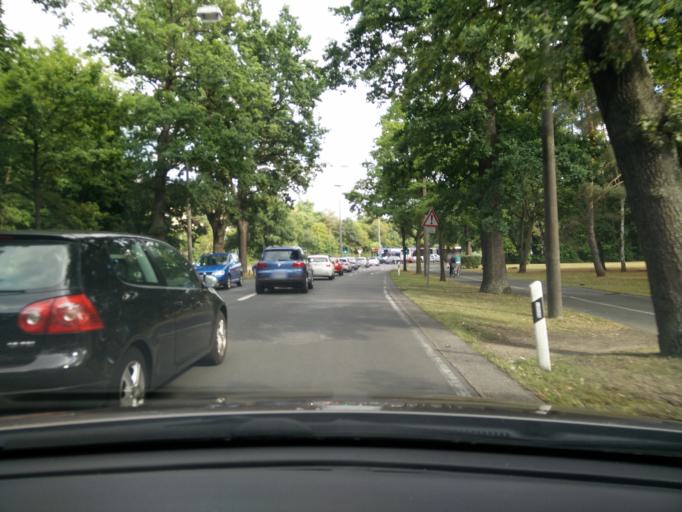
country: DE
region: Bavaria
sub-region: Regierungsbezirk Mittelfranken
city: Erlangen
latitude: 49.5778
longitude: 11.0150
